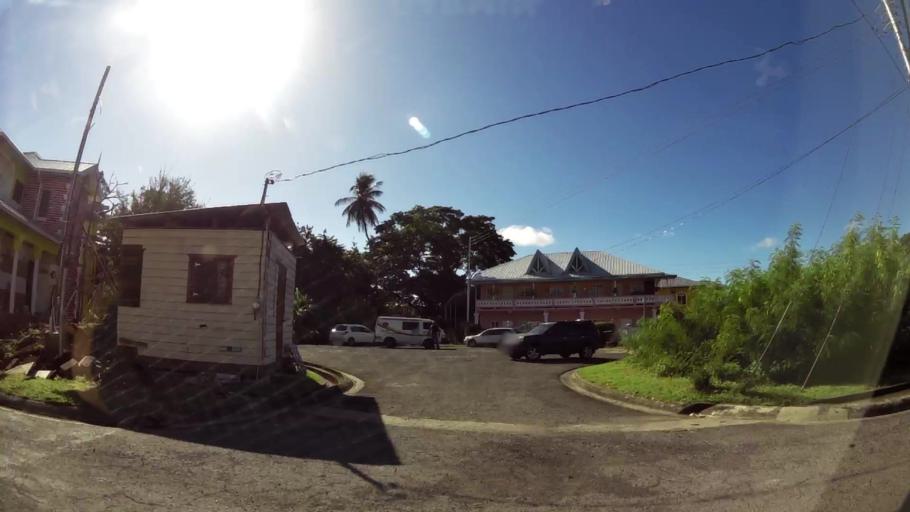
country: TT
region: Tobago
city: Scarborough
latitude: 11.1590
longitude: -60.8241
